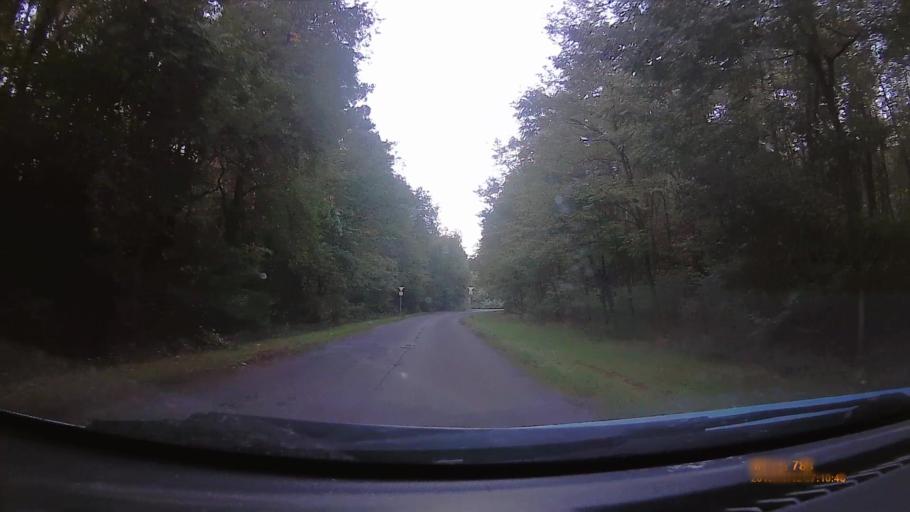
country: HU
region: Hajdu-Bihar
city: Mikepercs
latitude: 47.4633
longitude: 21.6765
